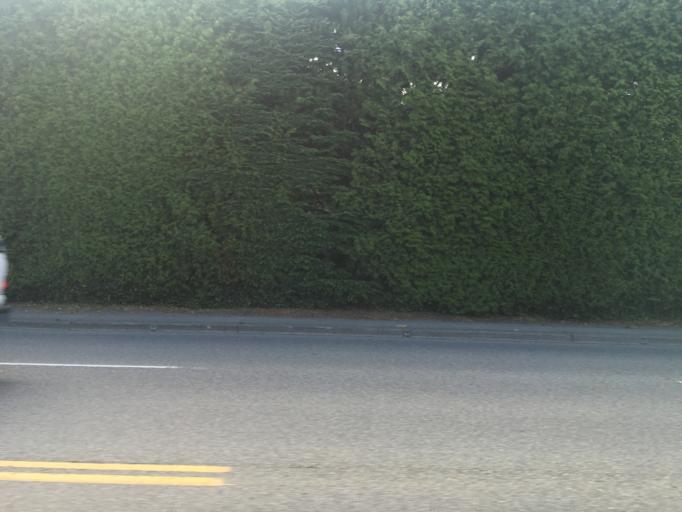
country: CA
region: British Columbia
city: Port Moody
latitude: 49.2462
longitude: -122.8724
